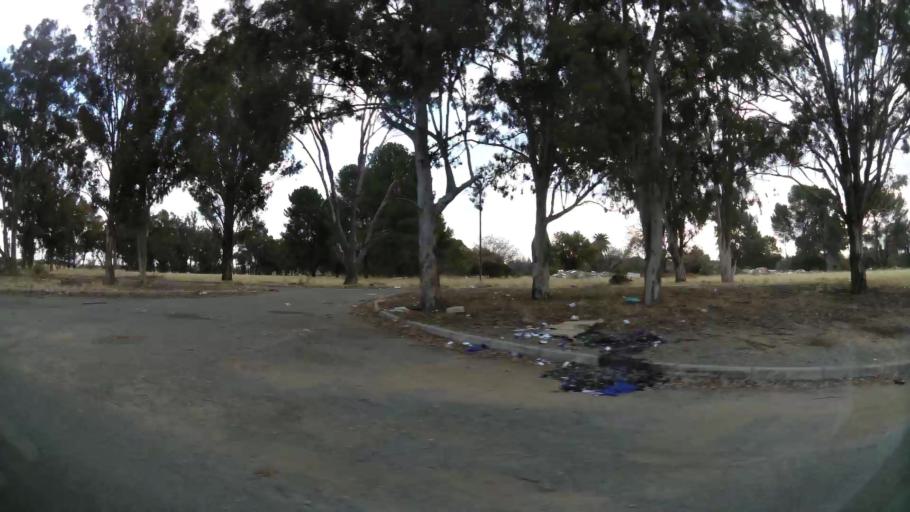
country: ZA
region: Orange Free State
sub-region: Lejweleputswa District Municipality
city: Welkom
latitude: -27.9986
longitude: 26.7193
